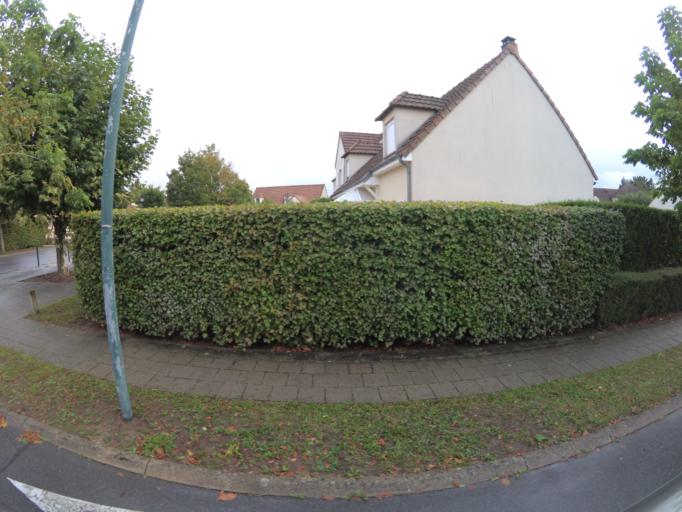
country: FR
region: Ile-de-France
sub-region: Departement de Seine-et-Marne
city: Chanteloup-en-Brie
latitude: 48.8578
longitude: 2.7366
